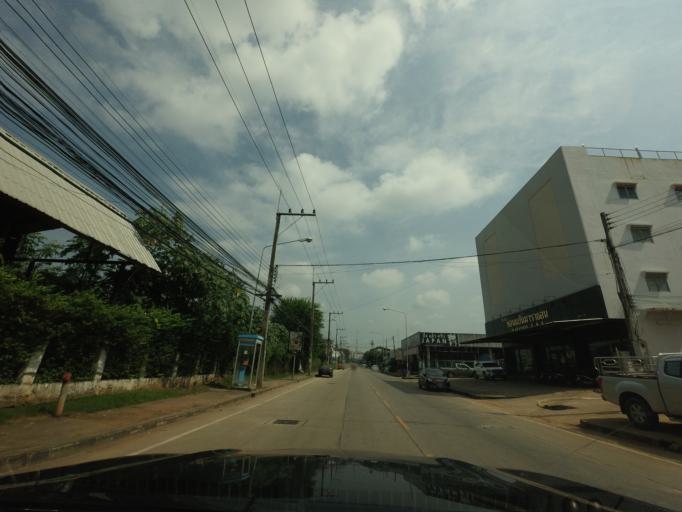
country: TH
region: Khon Kaen
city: Khon Kaen
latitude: 16.4333
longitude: 102.8293
